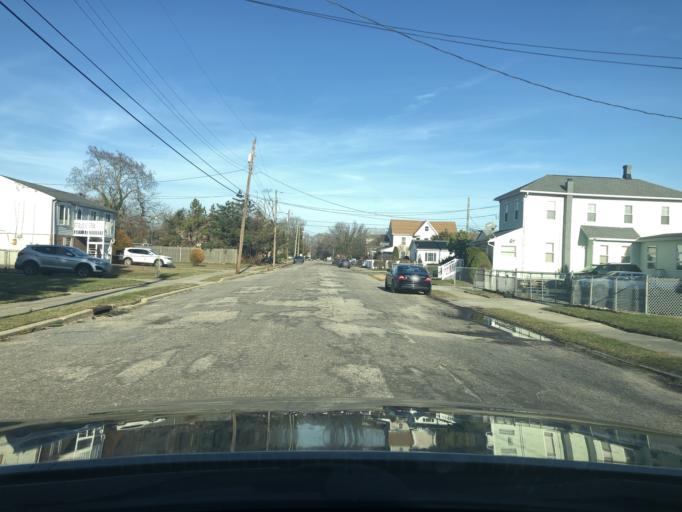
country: US
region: New Jersey
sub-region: Atlantic County
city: Northfield
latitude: 39.3832
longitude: -74.5411
